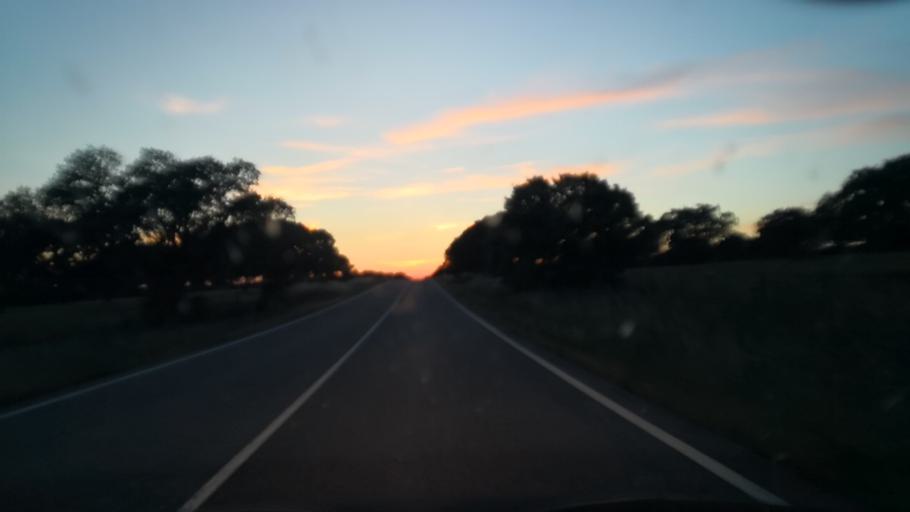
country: ES
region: Extremadura
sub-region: Provincia de Caceres
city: Piedras Albas
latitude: 39.7835
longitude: -6.9375
